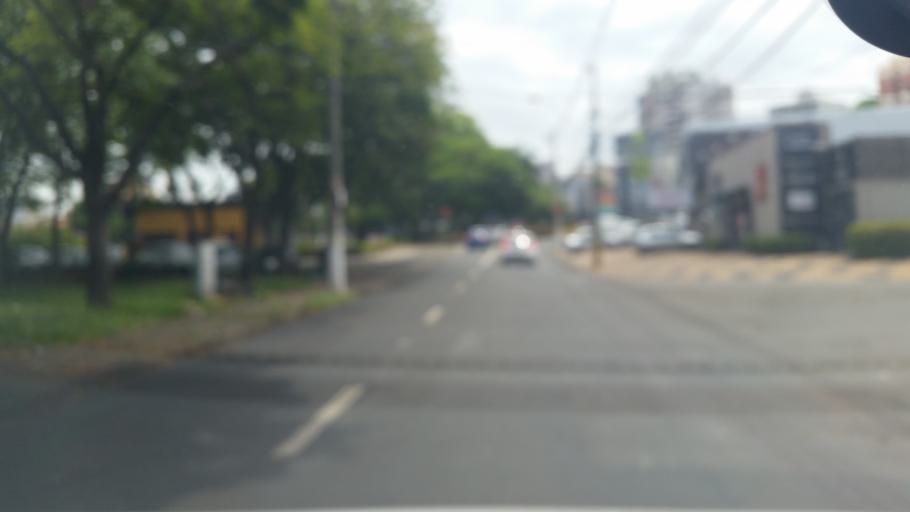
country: BR
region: Sao Paulo
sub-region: Campinas
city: Campinas
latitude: -22.8810
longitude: -47.0643
